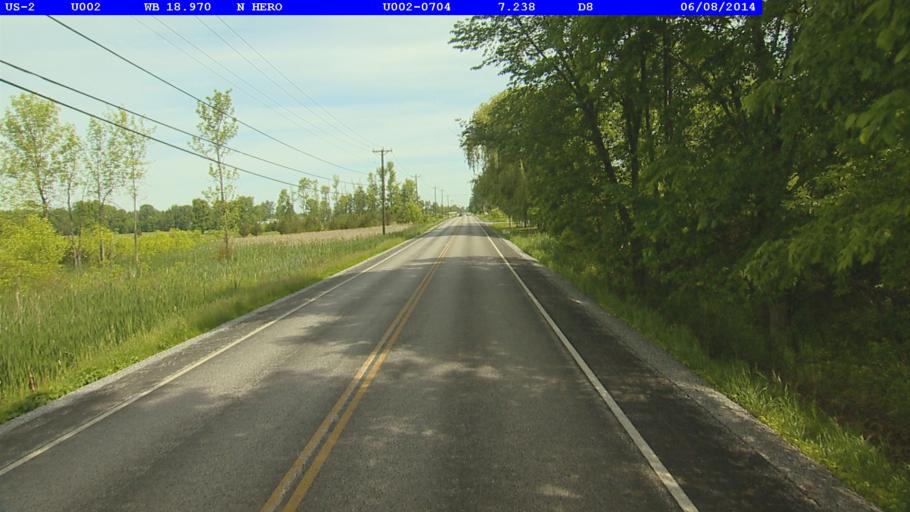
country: US
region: Vermont
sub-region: Grand Isle County
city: North Hero
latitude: 44.7954
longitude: -73.2924
